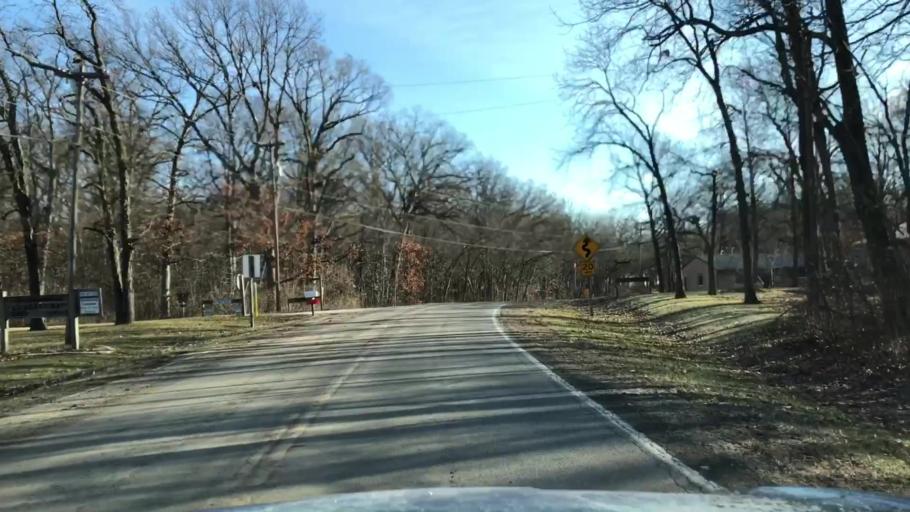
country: US
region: Illinois
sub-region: McLean County
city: Hudson
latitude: 40.6490
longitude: -88.9143
